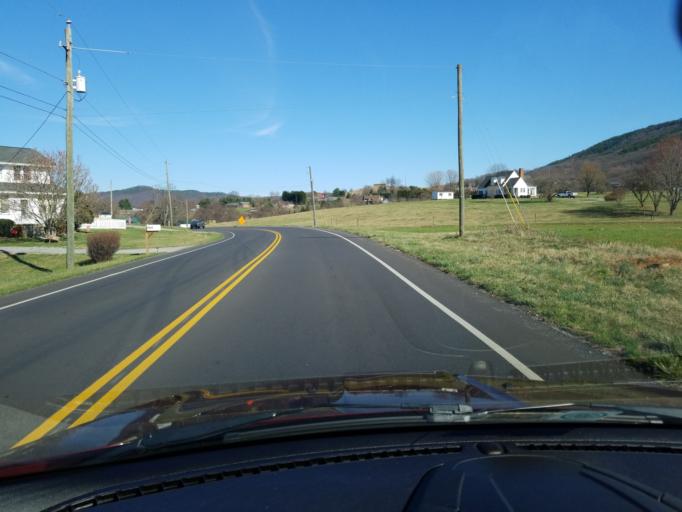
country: US
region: Virginia
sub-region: Botetourt County
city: Cloverdale
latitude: 37.3524
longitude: -79.9178
